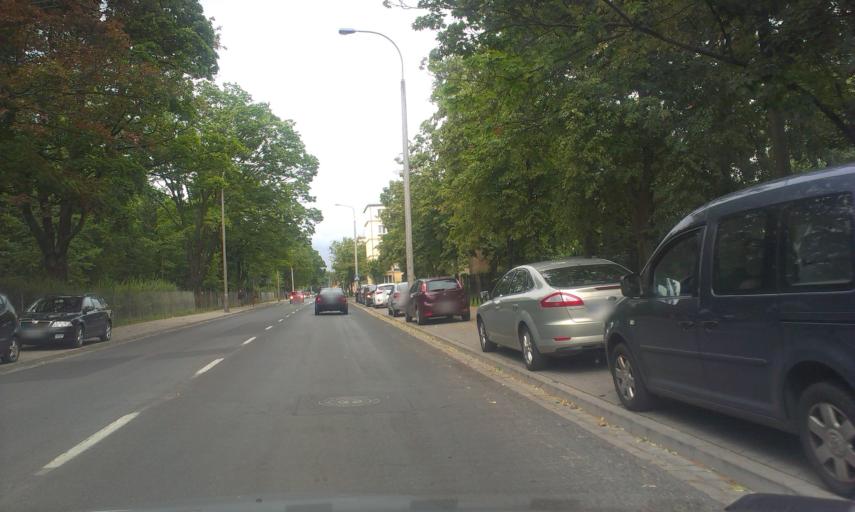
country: PL
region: Greater Poland Voivodeship
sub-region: Poznan
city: Poznan
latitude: 52.4136
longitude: 16.8786
